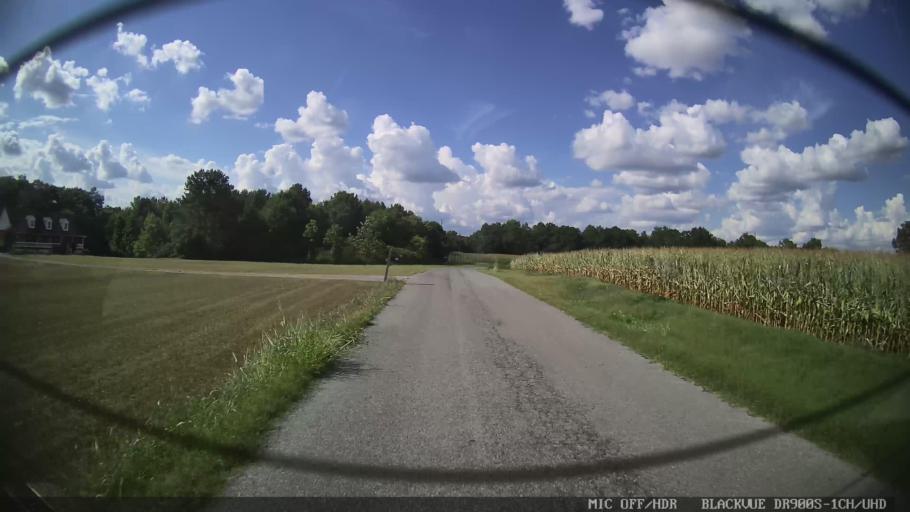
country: US
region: Georgia
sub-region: Bartow County
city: Euharlee
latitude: 34.0997
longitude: -84.9501
